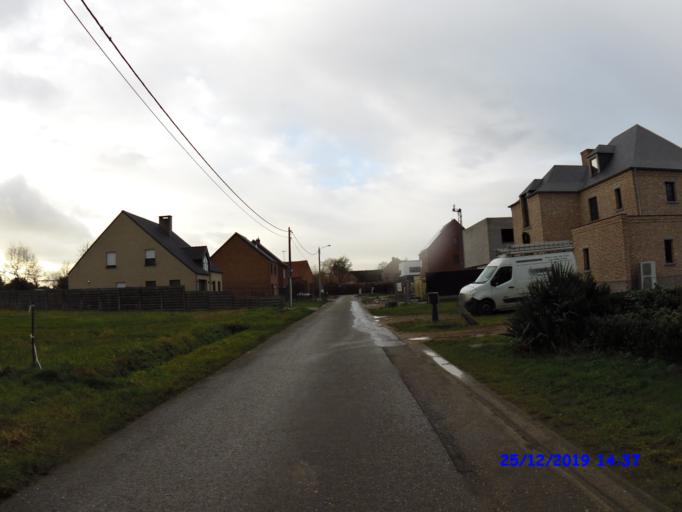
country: BE
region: Flanders
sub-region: Provincie Antwerpen
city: Geel
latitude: 51.1683
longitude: 4.9769
